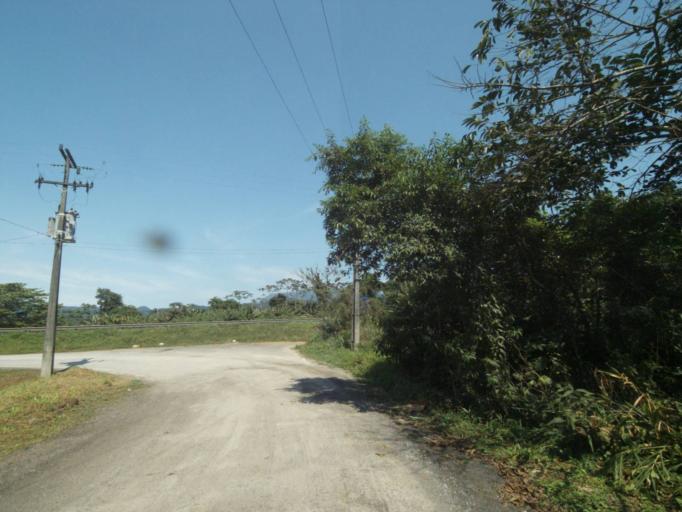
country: BR
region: Parana
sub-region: Antonina
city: Antonina
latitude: -25.5407
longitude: -48.6883
